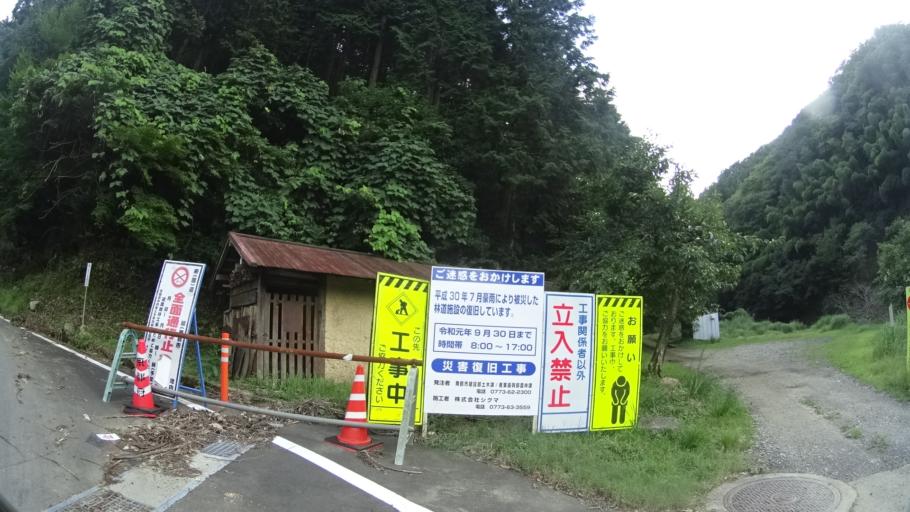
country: JP
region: Kyoto
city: Maizuru
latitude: 35.4006
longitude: 135.3496
